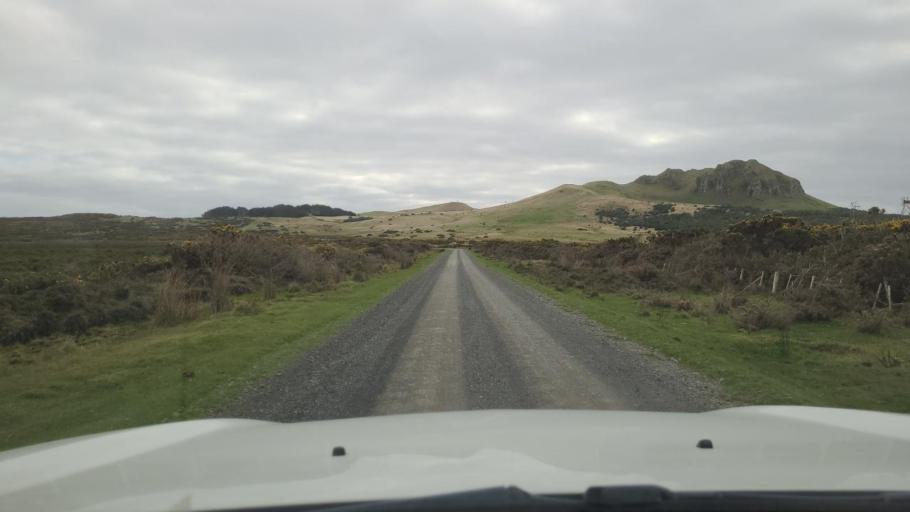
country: NZ
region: Chatham Islands
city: Waitangi
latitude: -43.7365
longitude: -176.5671
